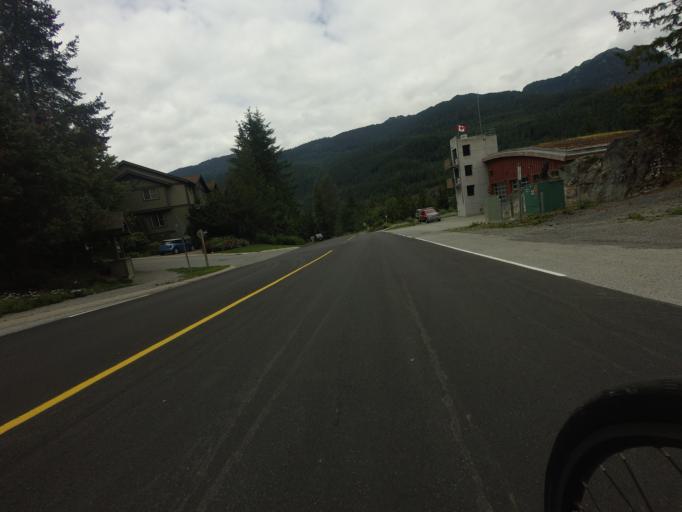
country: CA
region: British Columbia
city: Whistler
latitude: 50.0864
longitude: -123.0239
